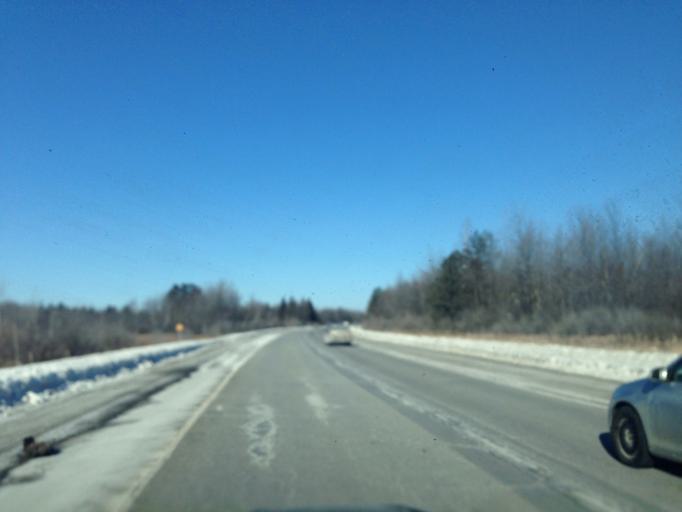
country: CA
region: Ontario
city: Ottawa
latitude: 45.3518
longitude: -75.4592
